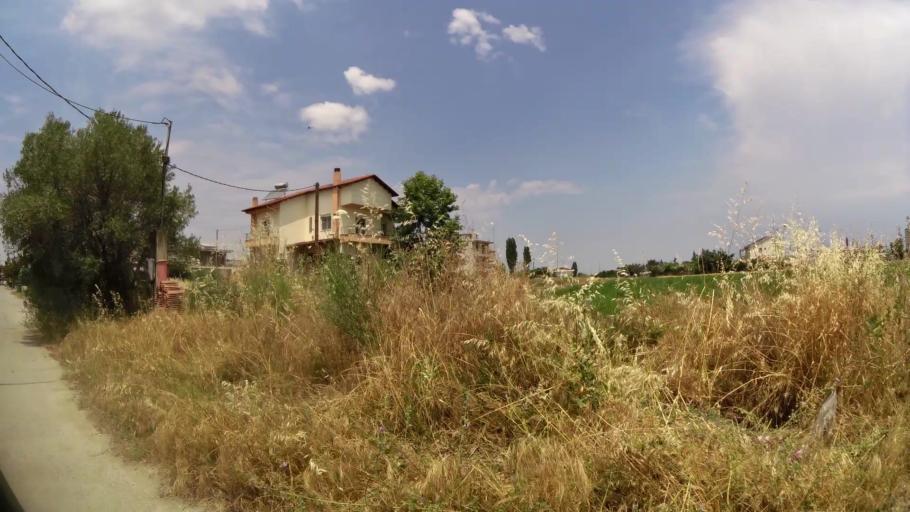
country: GR
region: Central Macedonia
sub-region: Nomos Pierias
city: Peristasi
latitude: 40.2712
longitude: 22.5455
